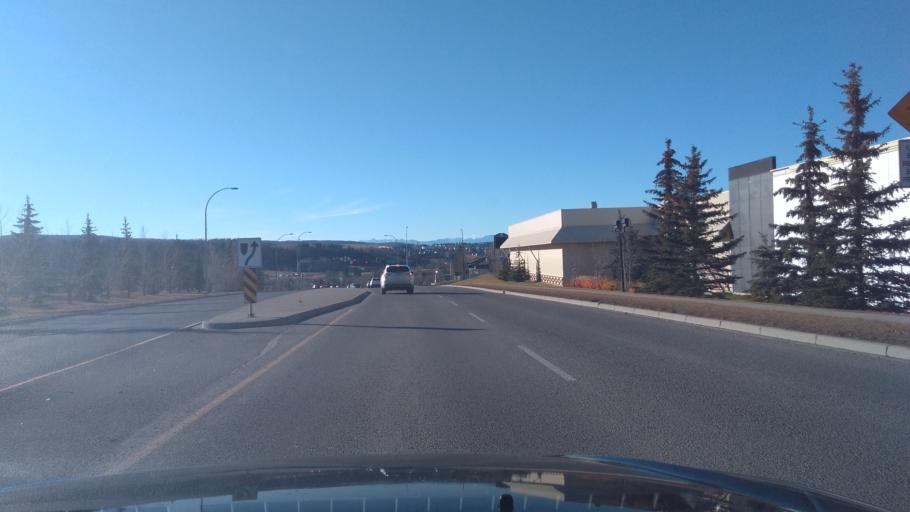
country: CA
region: Alberta
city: Cochrane
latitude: 51.1833
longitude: -114.4758
